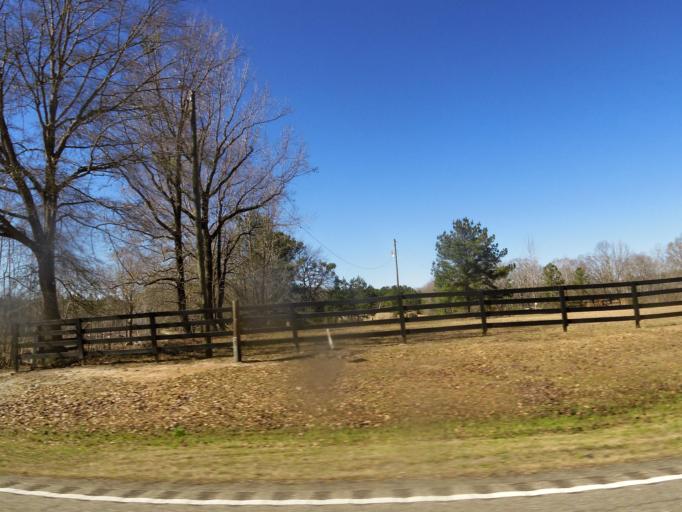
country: US
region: Alabama
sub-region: Bullock County
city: Union Springs
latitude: 32.1268
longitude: -85.7709
